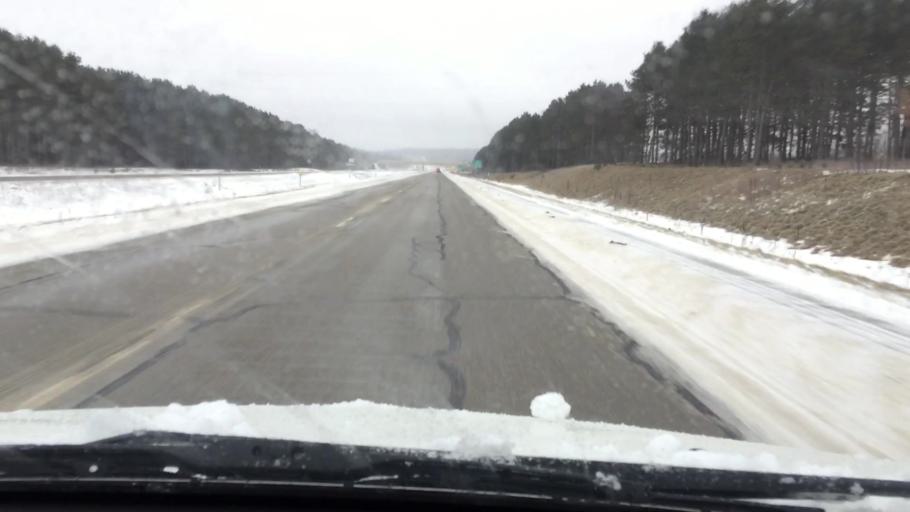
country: US
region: Michigan
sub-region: Wexford County
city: Cadillac
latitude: 44.2738
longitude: -85.3882
